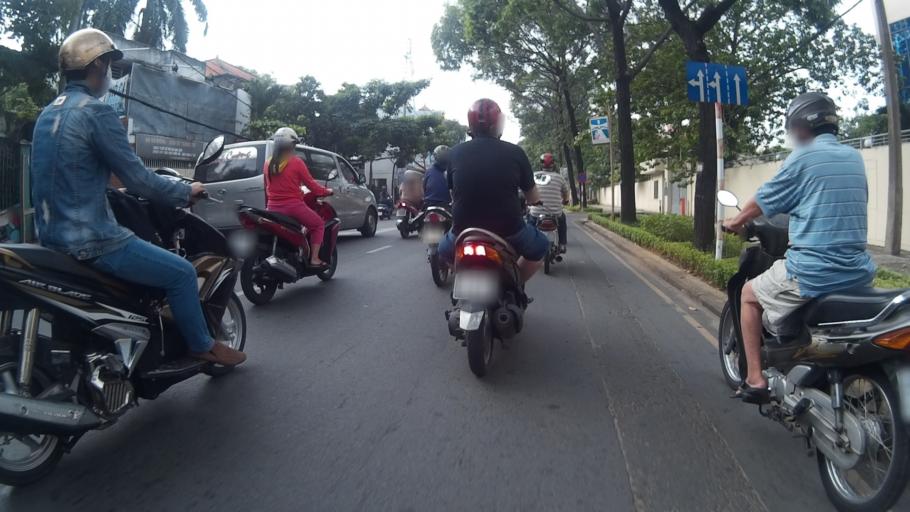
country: VN
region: Ho Chi Minh City
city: Quan Ba
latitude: 10.7809
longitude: 106.6851
